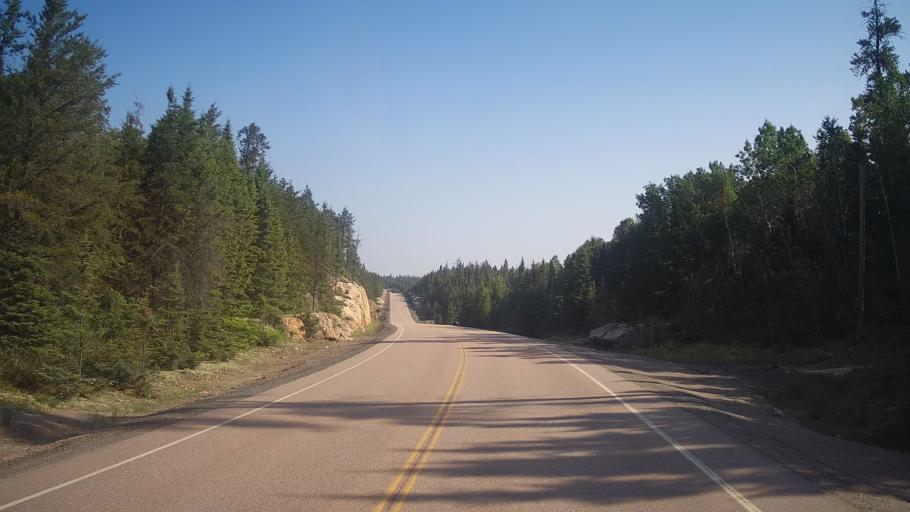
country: CA
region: Ontario
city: Rayside-Balfour
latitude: 47.0283
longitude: -81.6370
